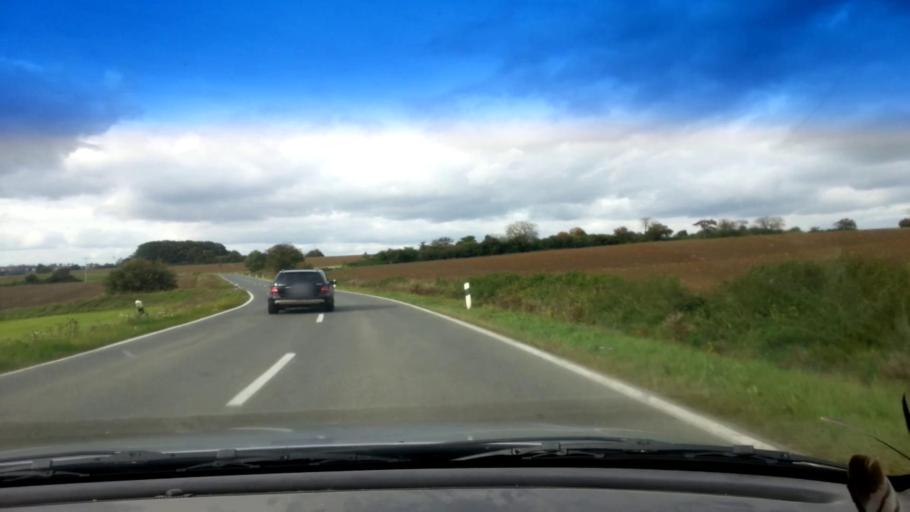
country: DE
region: Bavaria
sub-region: Upper Franconia
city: Schesslitz
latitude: 49.9795
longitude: 11.0218
